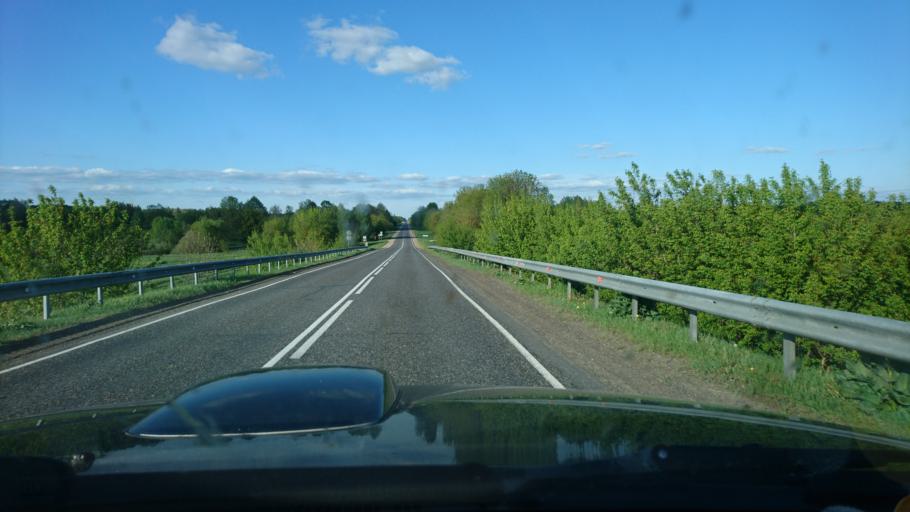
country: BY
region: Brest
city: Nyakhachava
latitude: 52.6400
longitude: 25.1974
